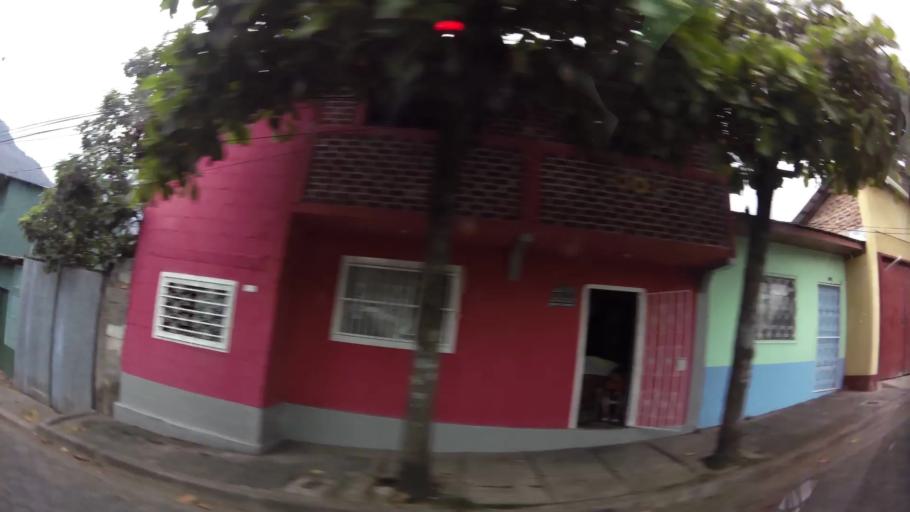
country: NI
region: Jinotega
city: Jinotega
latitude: 13.0898
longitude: -86.0034
